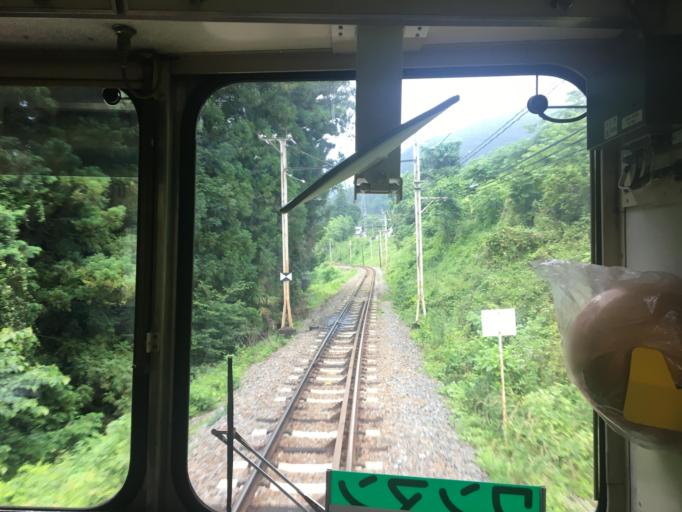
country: JP
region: Saitama
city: Chichibu
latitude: 35.9652
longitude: 139.0507
